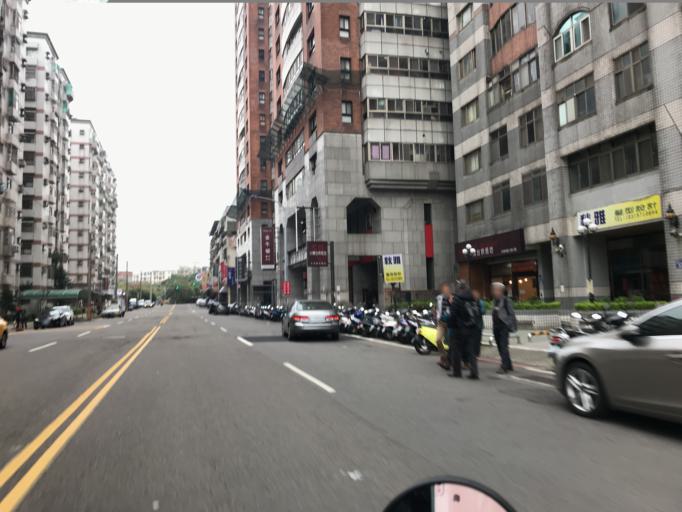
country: TW
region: Taiwan
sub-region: Hsinchu
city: Hsinchu
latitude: 24.8012
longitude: 120.9927
